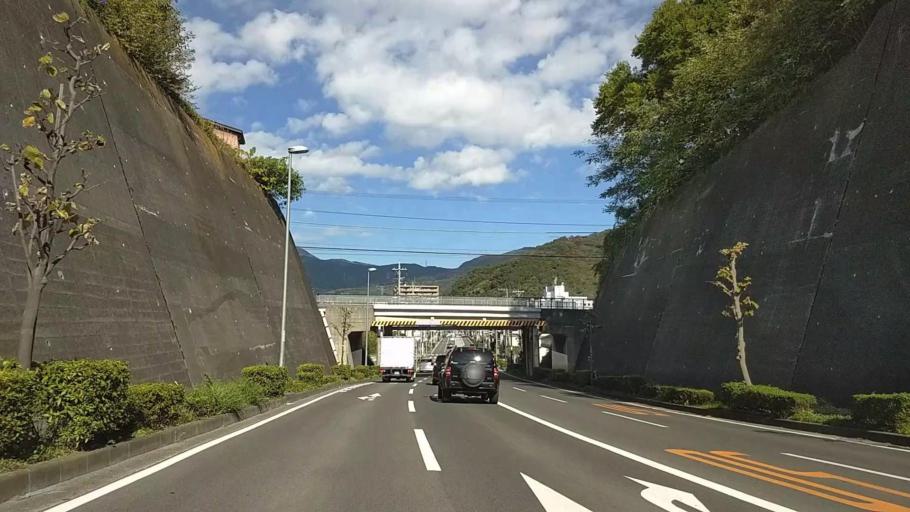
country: JP
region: Kanagawa
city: Hadano
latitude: 35.3645
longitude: 139.2340
